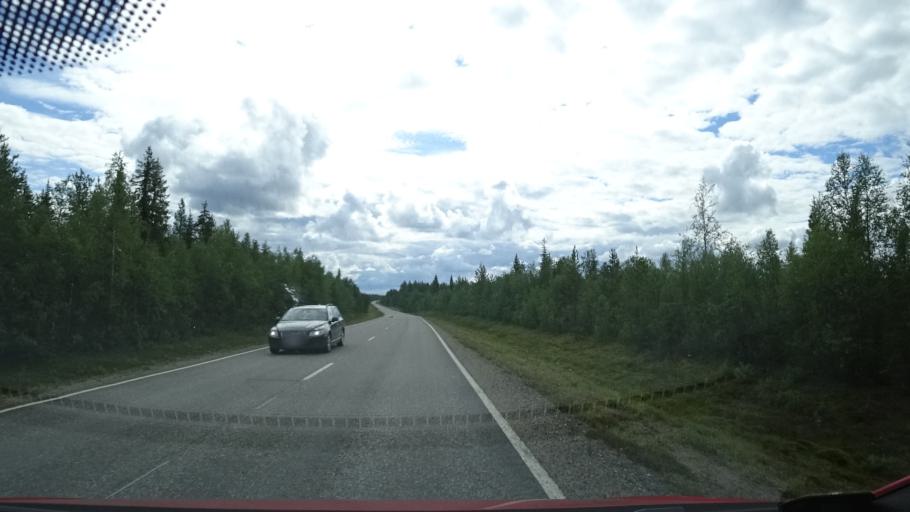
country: FI
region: Lapland
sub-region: Tunturi-Lappi
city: Kittilae
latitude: 67.5354
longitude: 24.9074
